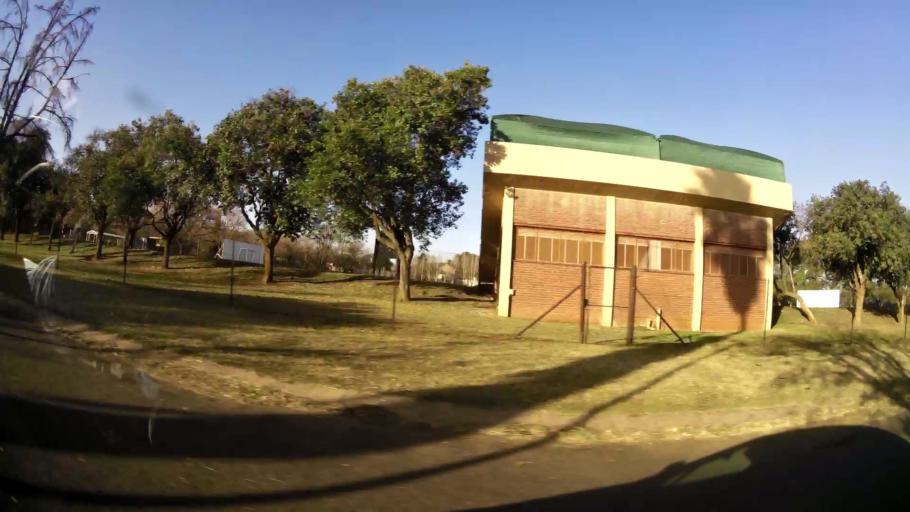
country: ZA
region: Gauteng
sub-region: City of Tshwane Metropolitan Municipality
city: Pretoria
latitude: -25.7062
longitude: 28.2021
